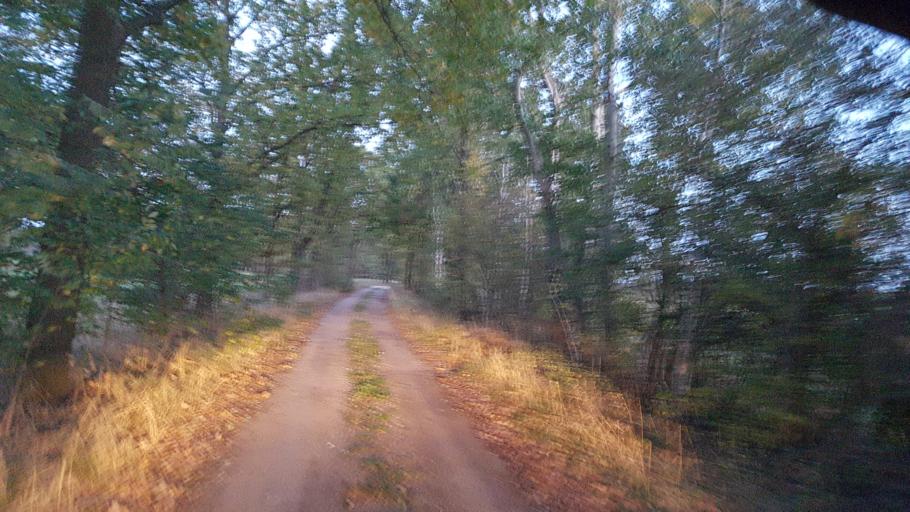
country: DE
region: Brandenburg
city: Doberlug-Kirchhain
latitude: 51.6438
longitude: 13.5860
